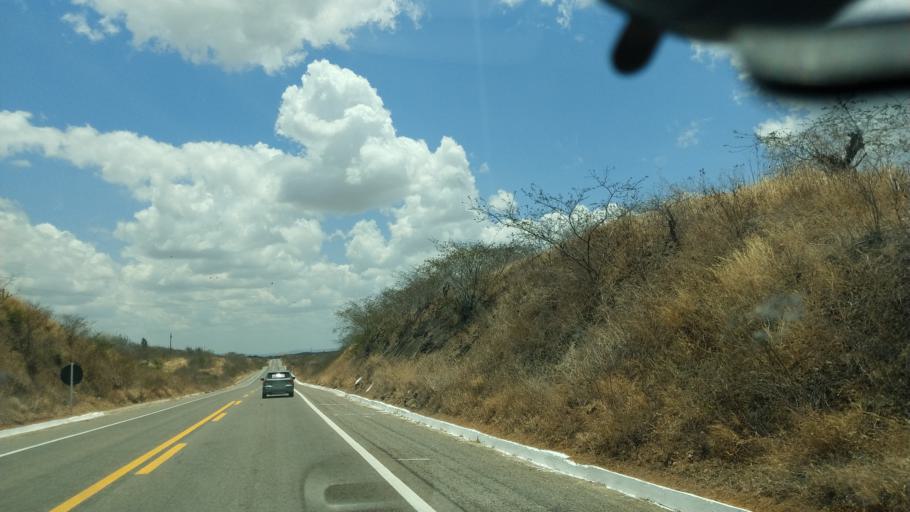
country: BR
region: Rio Grande do Norte
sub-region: Cerro Cora
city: Cerro Cora
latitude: -6.1927
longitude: -36.2595
